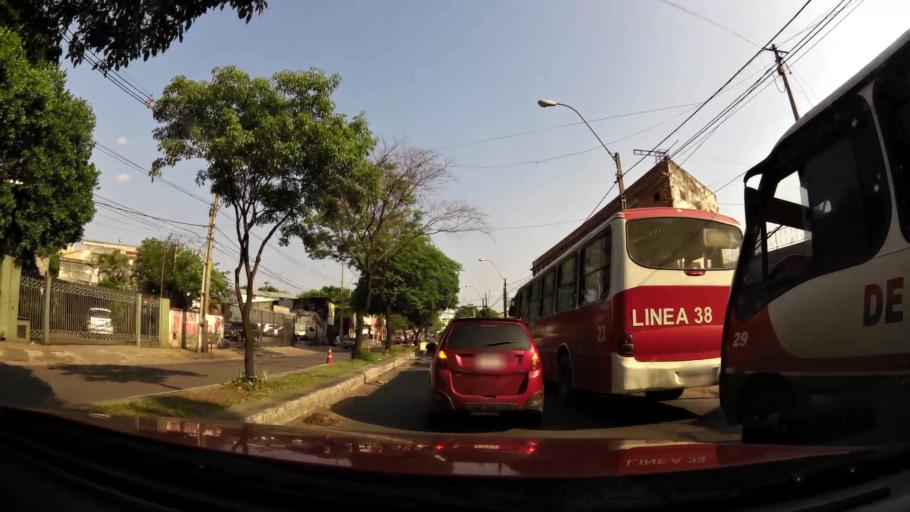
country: PY
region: Asuncion
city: Asuncion
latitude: -25.3049
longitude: -57.6197
